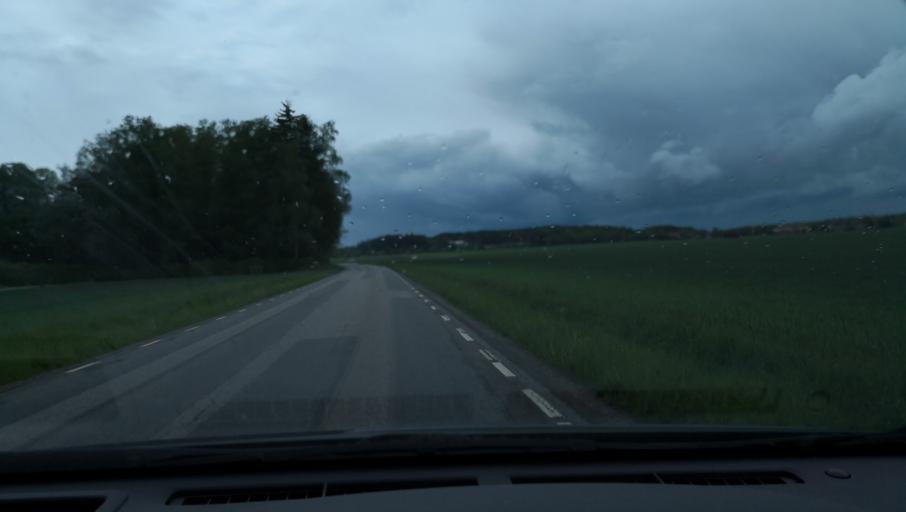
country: SE
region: Uppsala
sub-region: Enkopings Kommun
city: Orsundsbro
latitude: 59.7238
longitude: 17.3197
